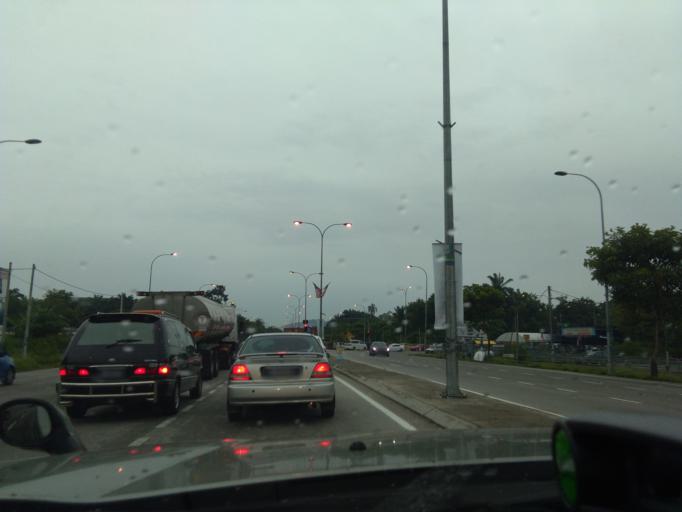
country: MY
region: Penang
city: Nibong Tebal
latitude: 5.1864
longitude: 100.4871
